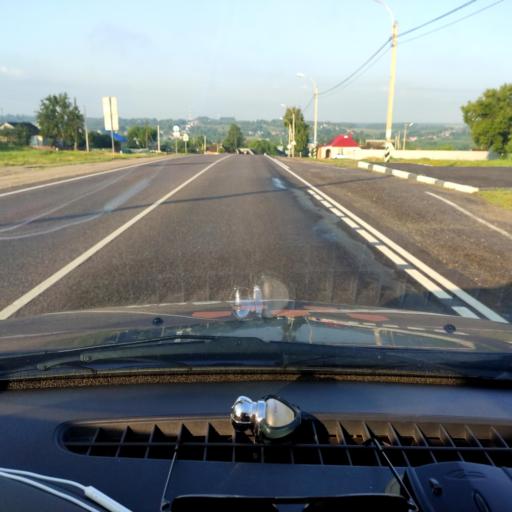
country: RU
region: Lipetsk
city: Kazaki
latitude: 52.6316
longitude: 38.2791
